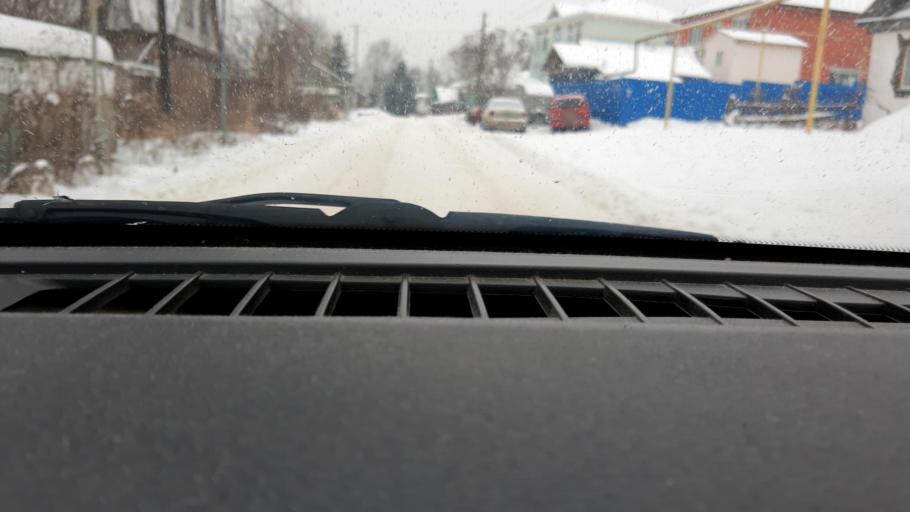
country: RU
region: Nizjnij Novgorod
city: Afonino
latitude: 56.1937
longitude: 44.0631
